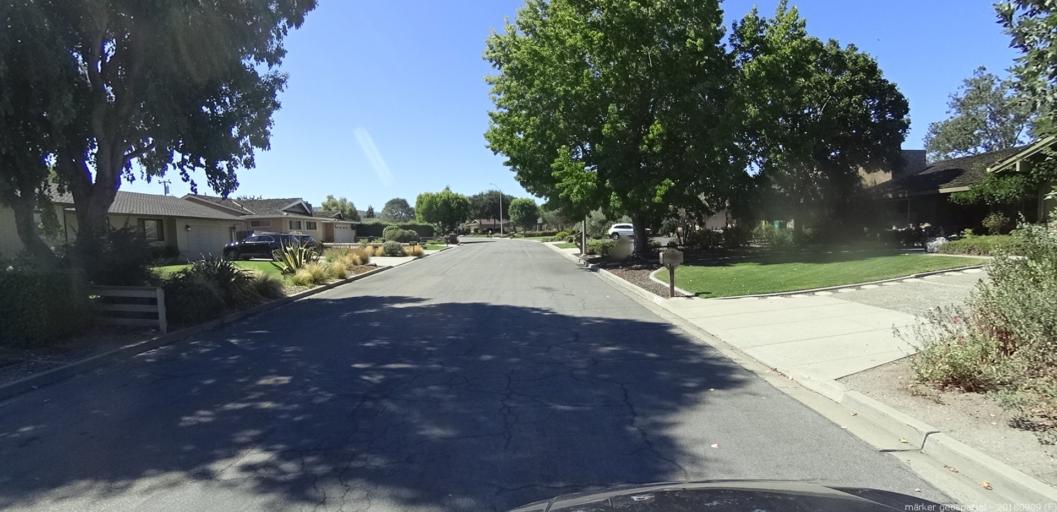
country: US
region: California
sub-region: Monterey County
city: Salinas
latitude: 36.6120
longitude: -121.6933
